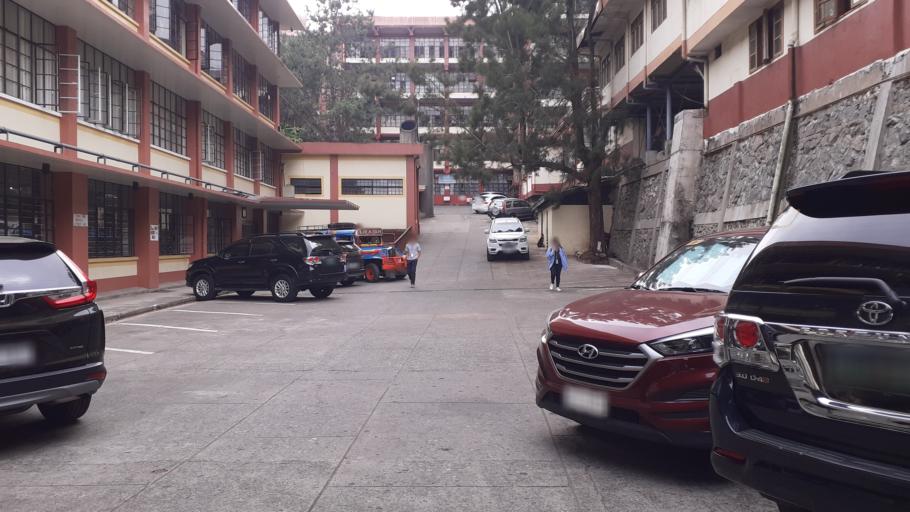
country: PH
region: Cordillera
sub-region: Baguio City
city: Baguio
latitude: 16.4177
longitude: 120.5983
